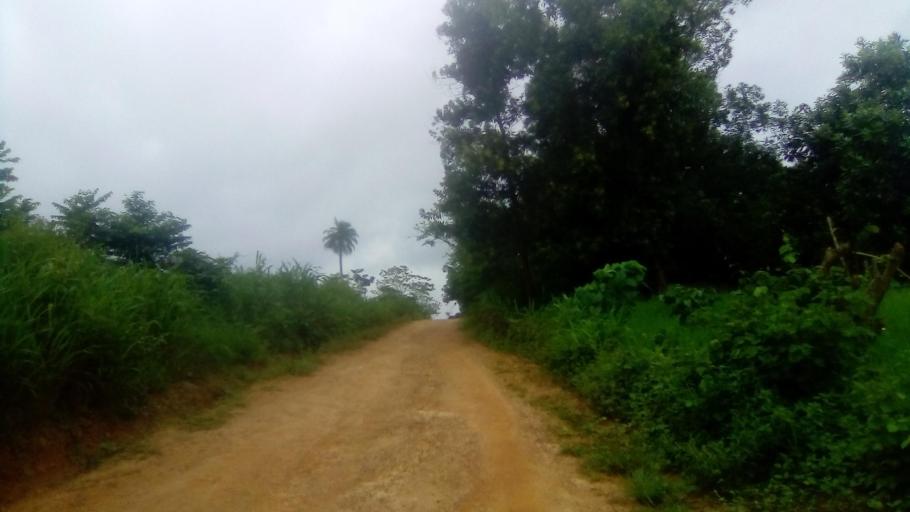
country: SL
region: Eastern Province
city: Kailahun
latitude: 8.2975
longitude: -10.5567
